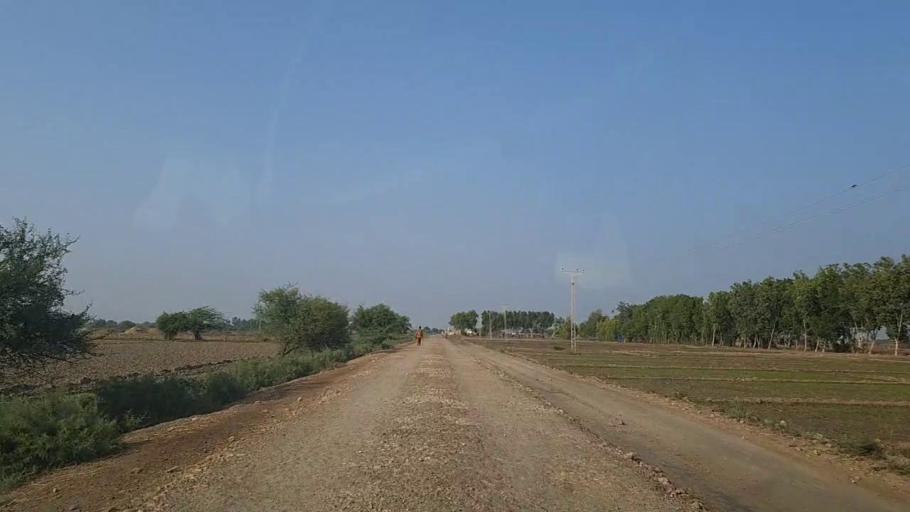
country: PK
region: Sindh
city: Mirpur Sakro
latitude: 24.5654
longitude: 67.6700
